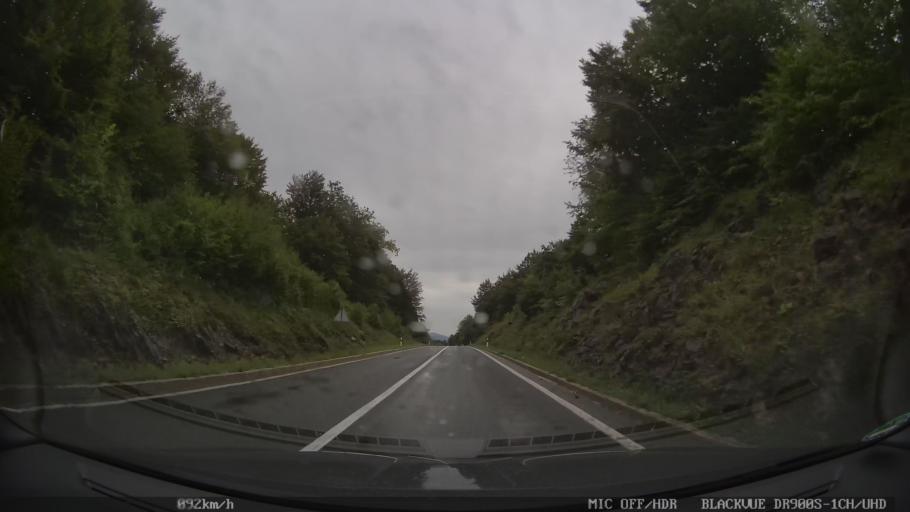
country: HR
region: Licko-Senjska
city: Brinje
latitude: 44.9631
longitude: 15.0828
